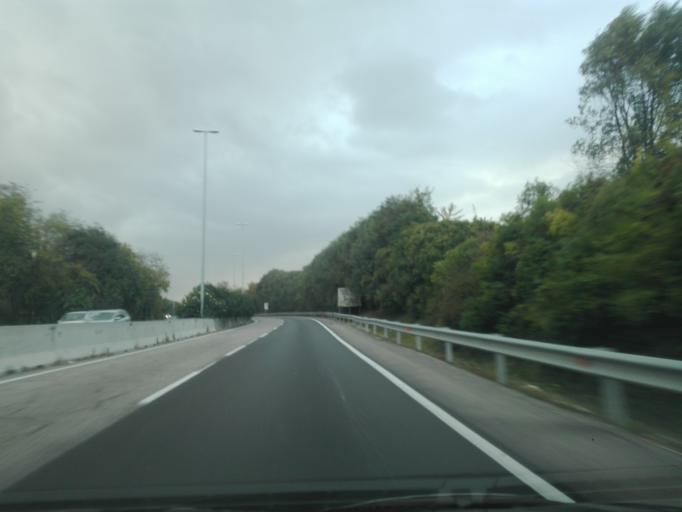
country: IT
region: Veneto
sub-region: Provincia di Verona
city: Verona
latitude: 45.4328
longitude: 10.9538
